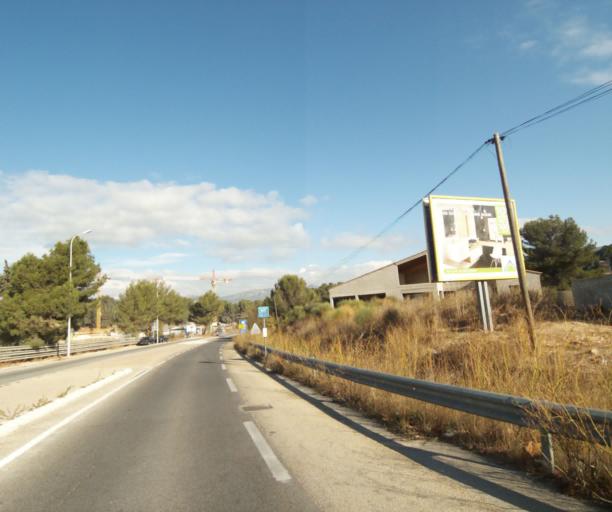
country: FR
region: Provence-Alpes-Cote d'Azur
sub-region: Departement des Bouches-du-Rhone
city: Allauch
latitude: 43.3205
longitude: 5.4686
